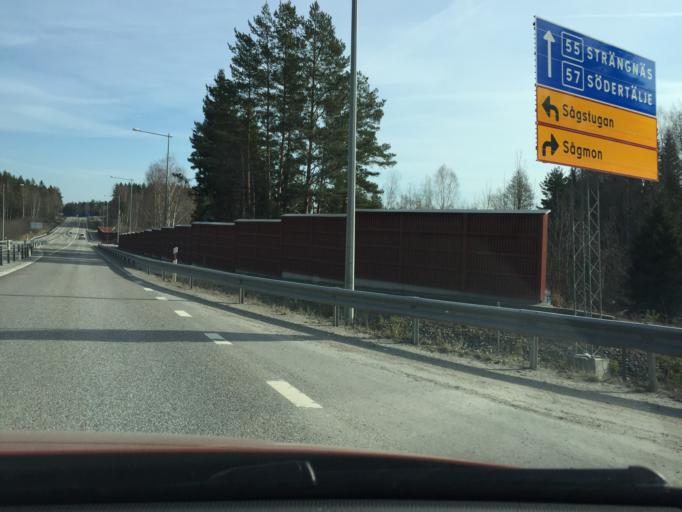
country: SE
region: Soedermanland
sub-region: Katrineholms Kommun
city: Katrineholm
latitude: 59.0111
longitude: 16.2586
